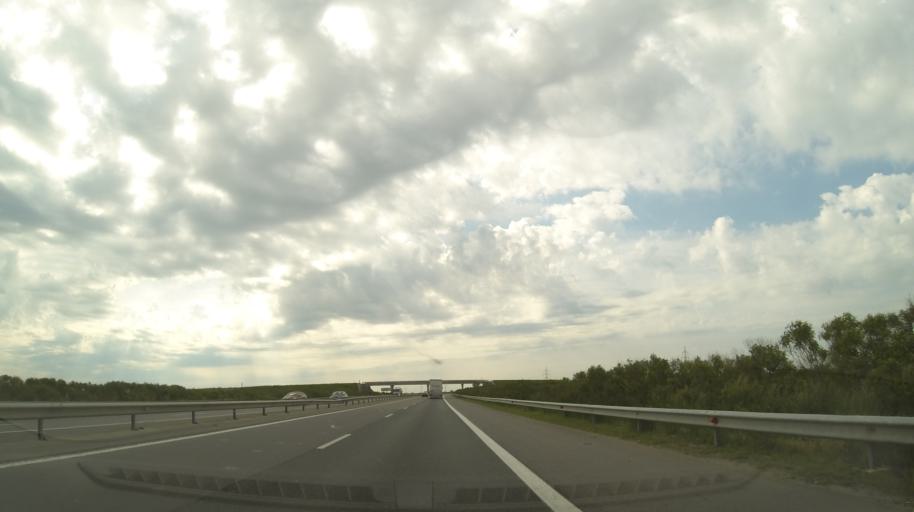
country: RO
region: Arges
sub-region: Comuna Ratesti
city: Ratesti
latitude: 44.7187
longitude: 25.1386
